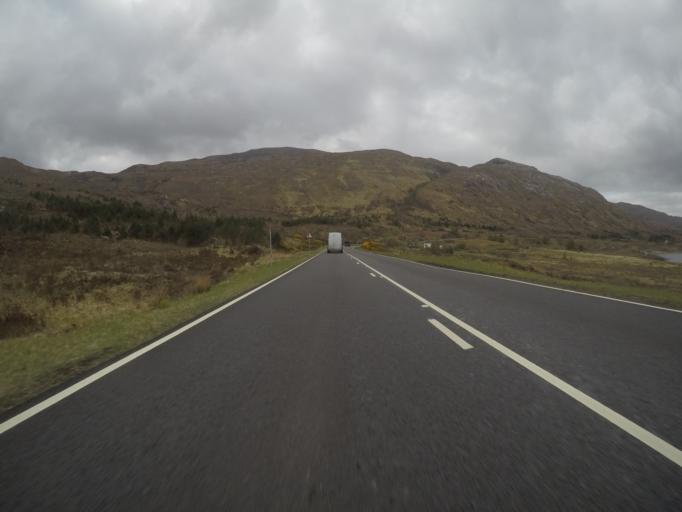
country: GB
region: Scotland
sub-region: Highland
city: Spean Bridge
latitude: 57.1447
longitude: -5.0691
